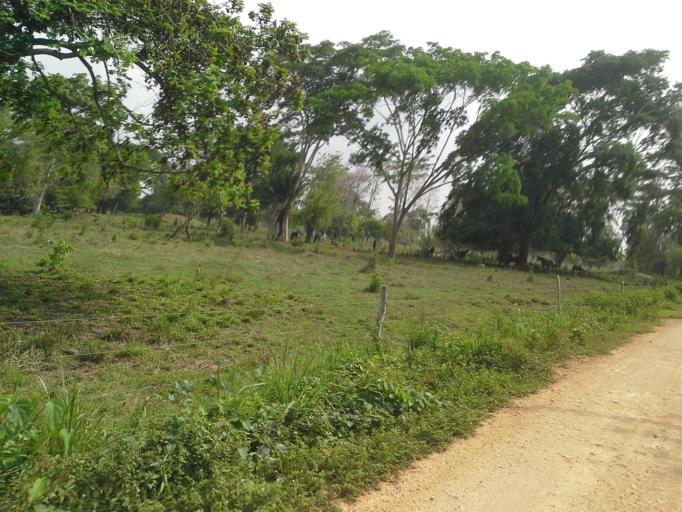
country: CO
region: Cordoba
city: Chima
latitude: 9.1771
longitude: -75.6133
